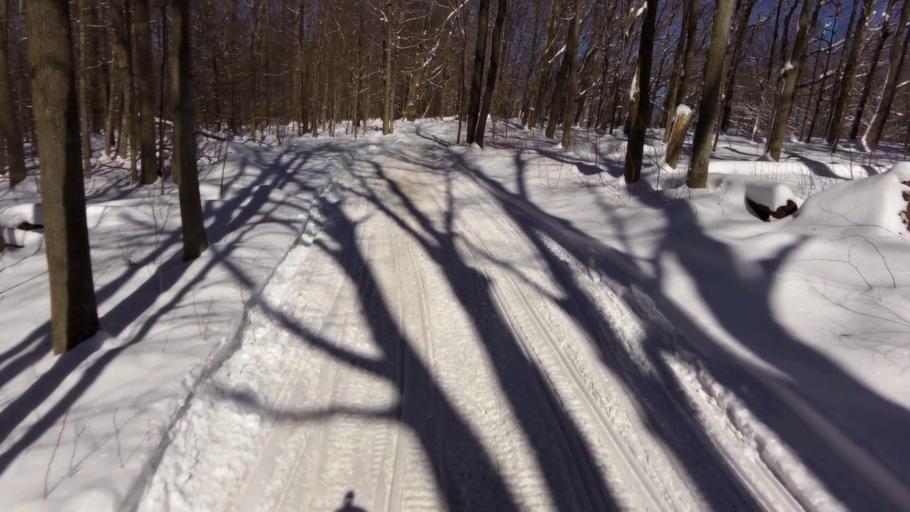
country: US
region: New York
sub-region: Chautauqua County
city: Mayville
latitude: 42.2452
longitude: -79.4193
